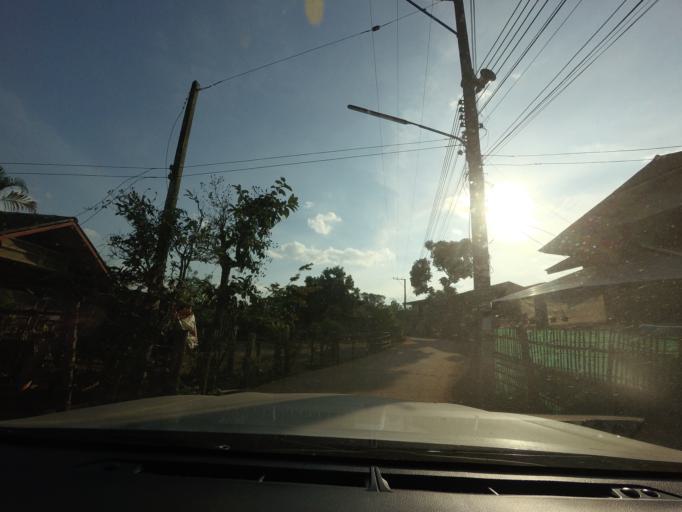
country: TH
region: Mae Hong Son
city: Wiang Nuea
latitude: 19.3978
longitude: 98.4045
